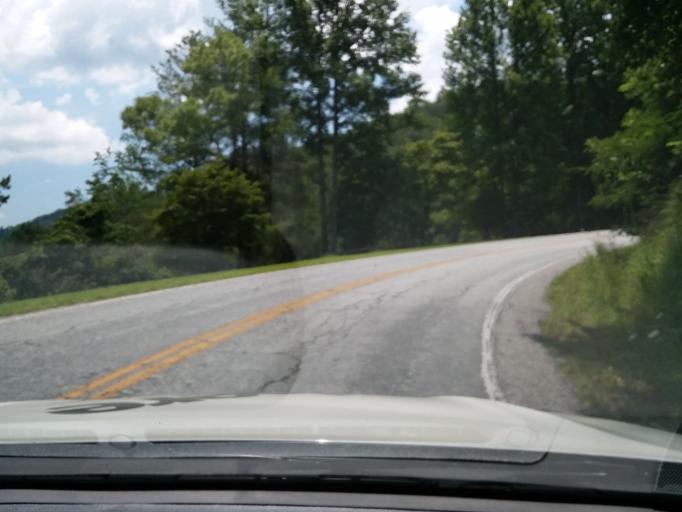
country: US
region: Georgia
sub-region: Rabun County
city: Mountain City
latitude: 34.9813
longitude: -83.1866
